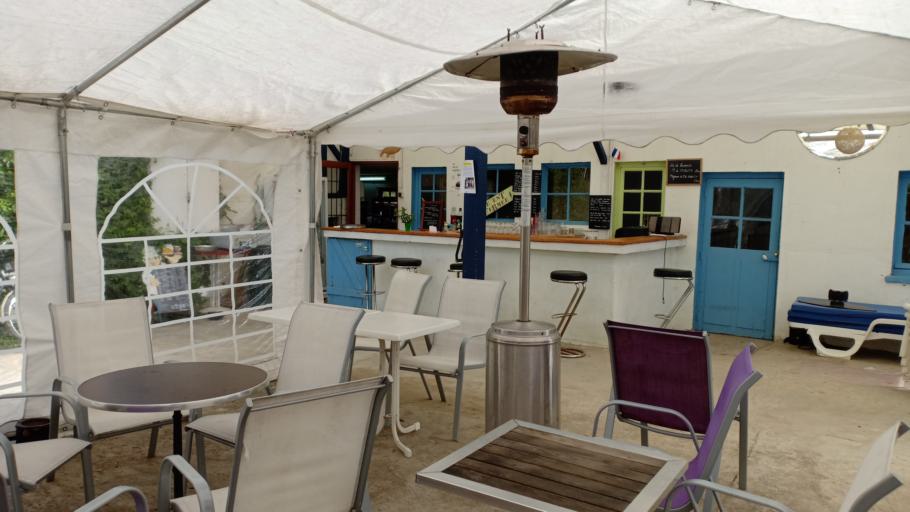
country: FR
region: Ile-de-France
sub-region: Departement des Yvelines
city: Medan
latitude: 48.9490
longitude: 1.9999
